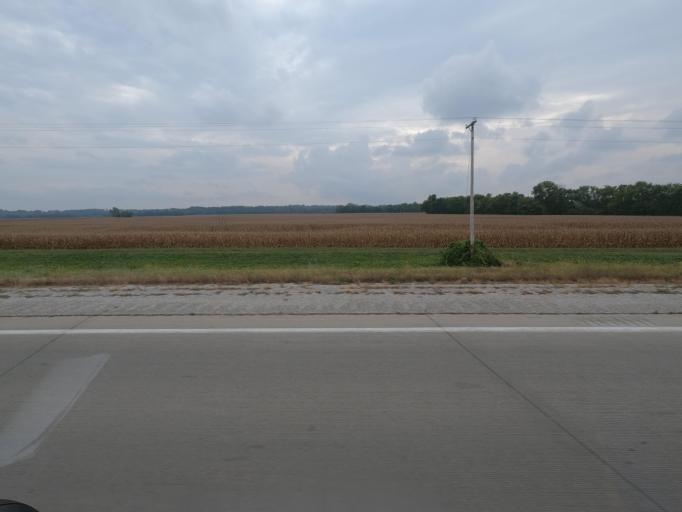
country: US
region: Iowa
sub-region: Wapello County
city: Eddyville
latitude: 41.1428
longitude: -92.6135
